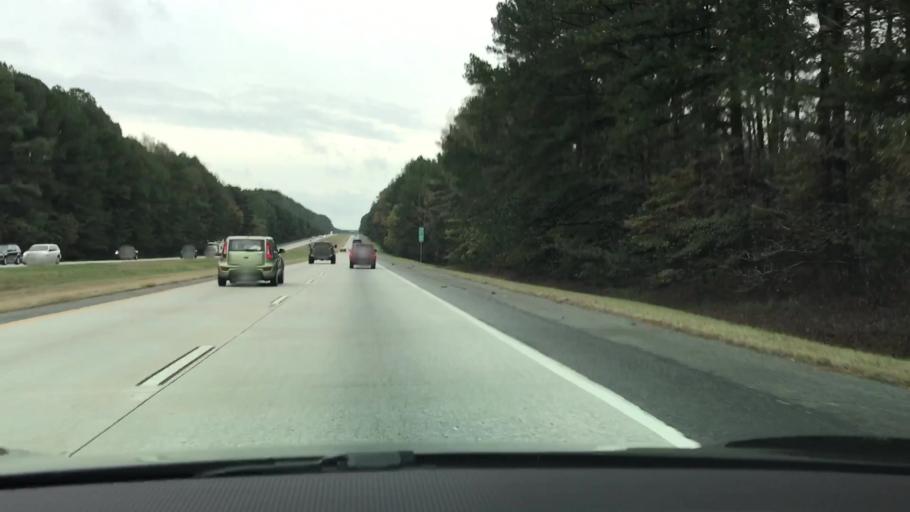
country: US
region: Georgia
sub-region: Greene County
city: Union Point
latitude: 33.5440
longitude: -83.0238
